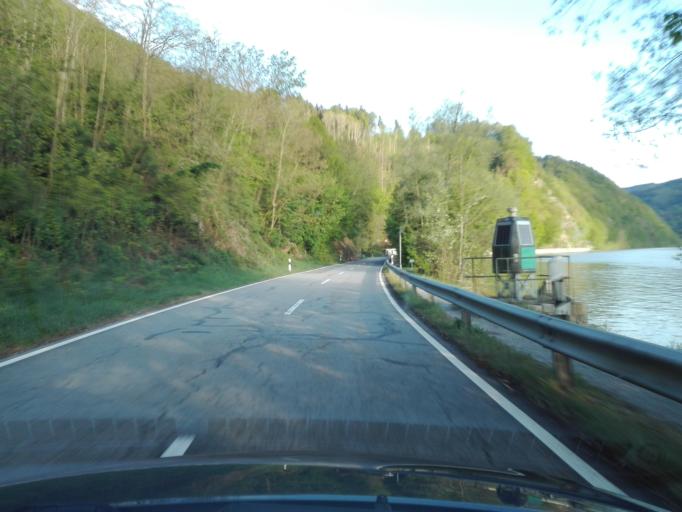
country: DE
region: Bavaria
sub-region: Lower Bavaria
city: Obernzell
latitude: 48.5515
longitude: 13.6526
